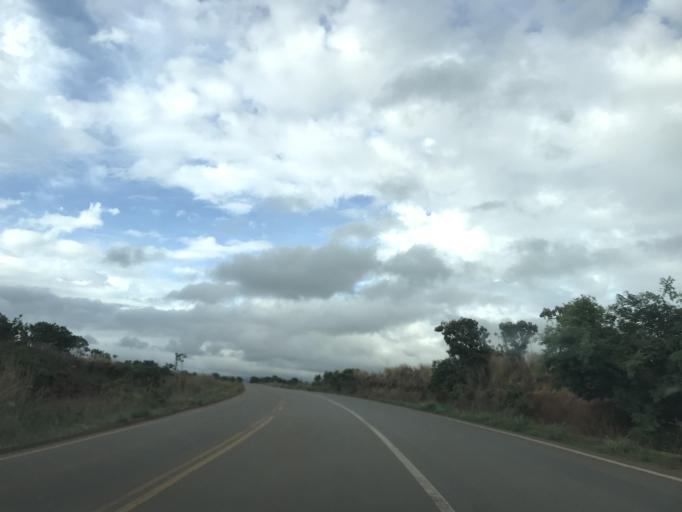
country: BR
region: Goias
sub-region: Vianopolis
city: Vianopolis
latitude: -16.5759
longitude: -48.2955
